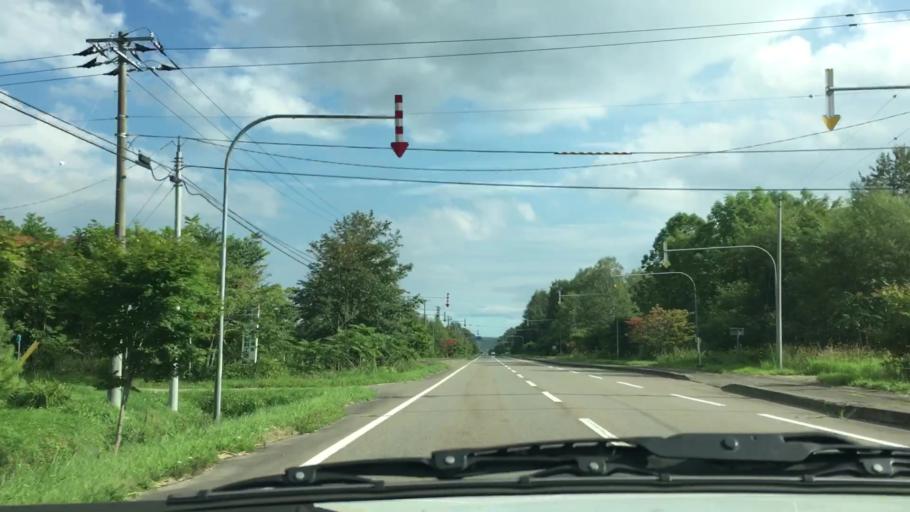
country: JP
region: Hokkaido
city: Otofuke
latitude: 43.3227
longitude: 143.3009
